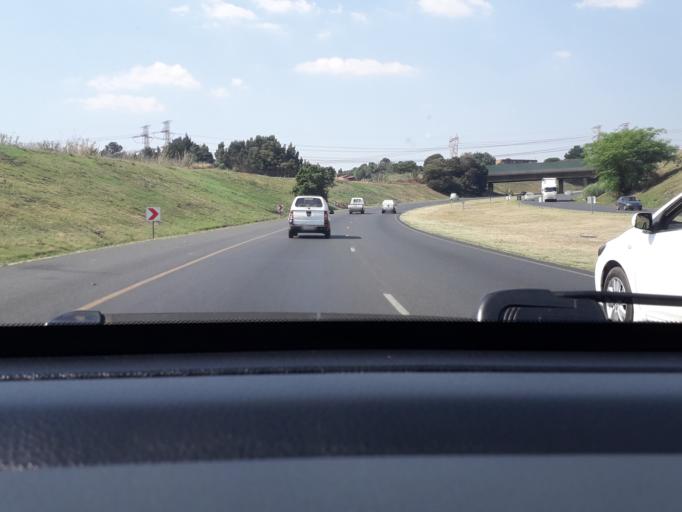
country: ZA
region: Gauteng
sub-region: City of Johannesburg Metropolitan Municipality
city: Modderfontein
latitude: -26.0924
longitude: 28.1856
